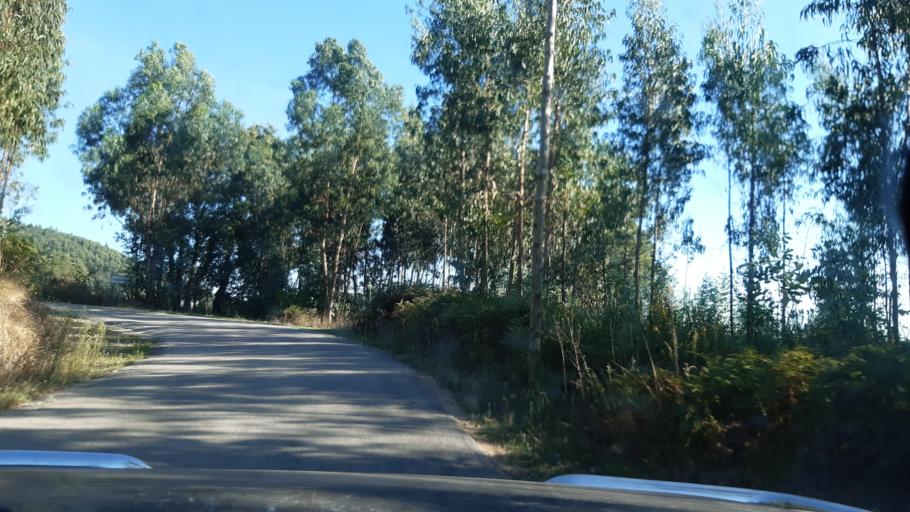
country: PT
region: Aveiro
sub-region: Agueda
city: Aguada de Cima
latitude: 40.5644
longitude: -8.3538
